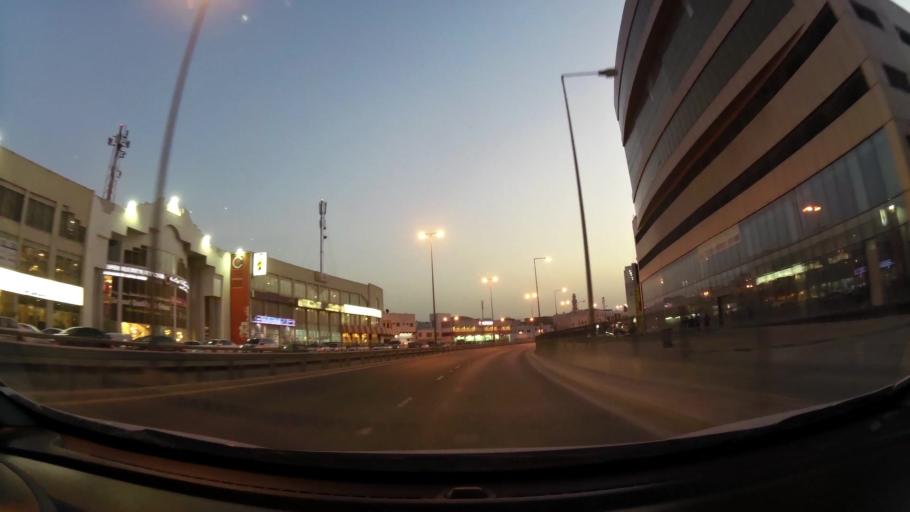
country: BH
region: Manama
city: Jidd Hafs
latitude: 26.2091
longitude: 50.5539
